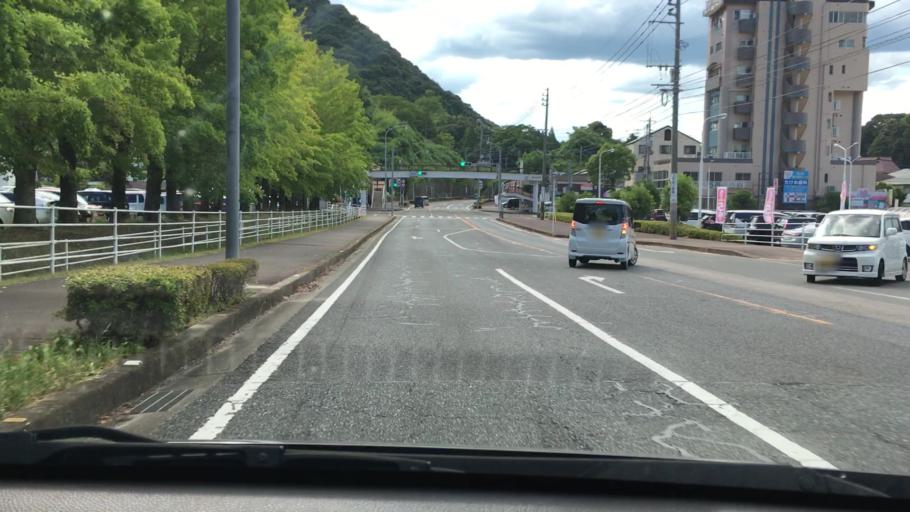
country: JP
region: Saga Prefecture
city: Takeocho-takeo
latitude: 33.1874
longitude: 130.0253
